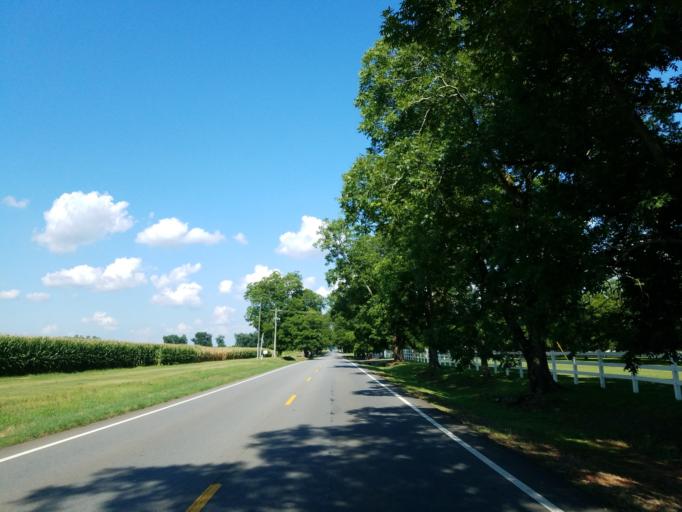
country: US
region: Georgia
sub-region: Peach County
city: Fort Valley
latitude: 32.5539
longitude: -83.8118
